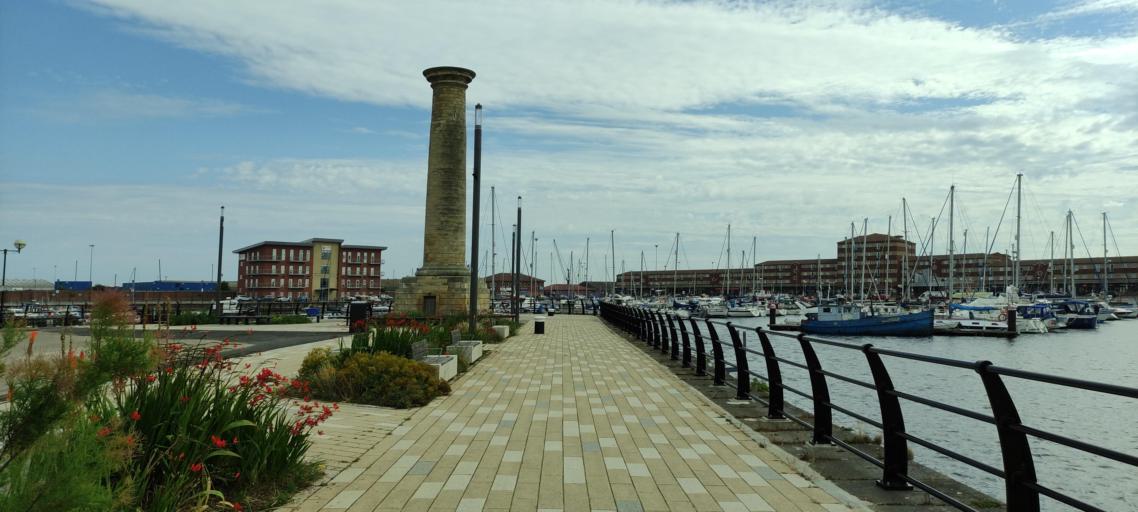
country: GB
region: England
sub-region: Hartlepool
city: Hartlepool
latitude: 54.6912
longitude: -1.2027
